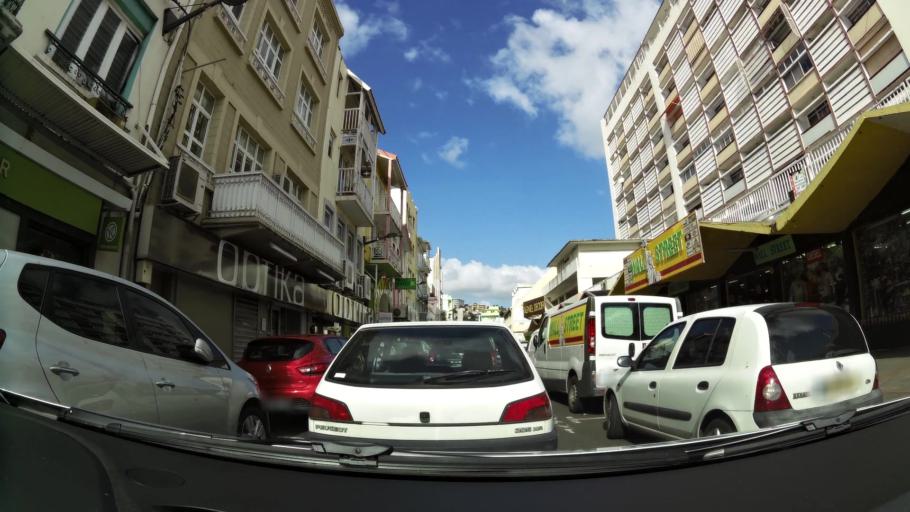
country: MQ
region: Martinique
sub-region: Martinique
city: Fort-de-France
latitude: 14.6056
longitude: -61.0688
